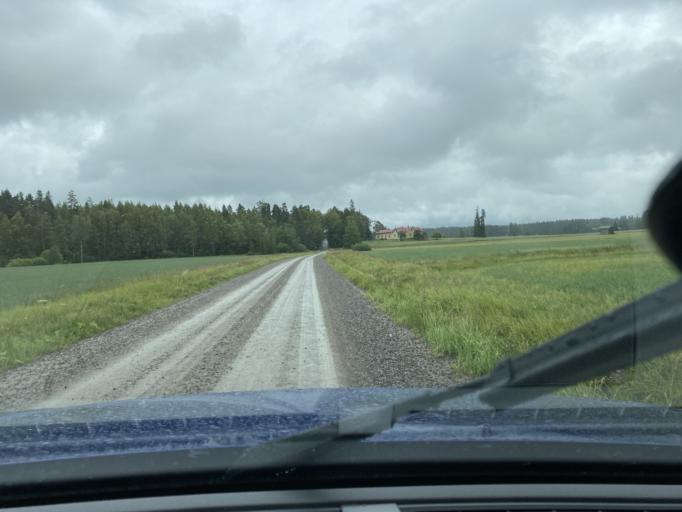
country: FI
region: Pirkanmaa
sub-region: Lounais-Pirkanmaa
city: Punkalaidun
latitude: 61.1489
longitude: 23.2235
